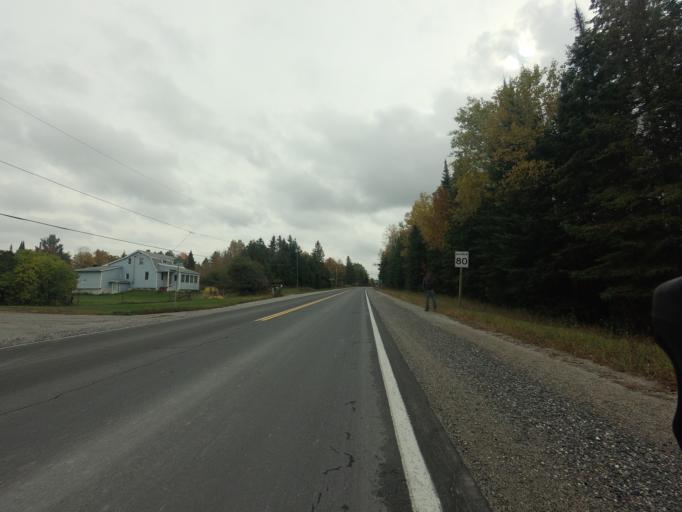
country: CA
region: Ontario
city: Perth
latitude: 45.1198
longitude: -76.4944
